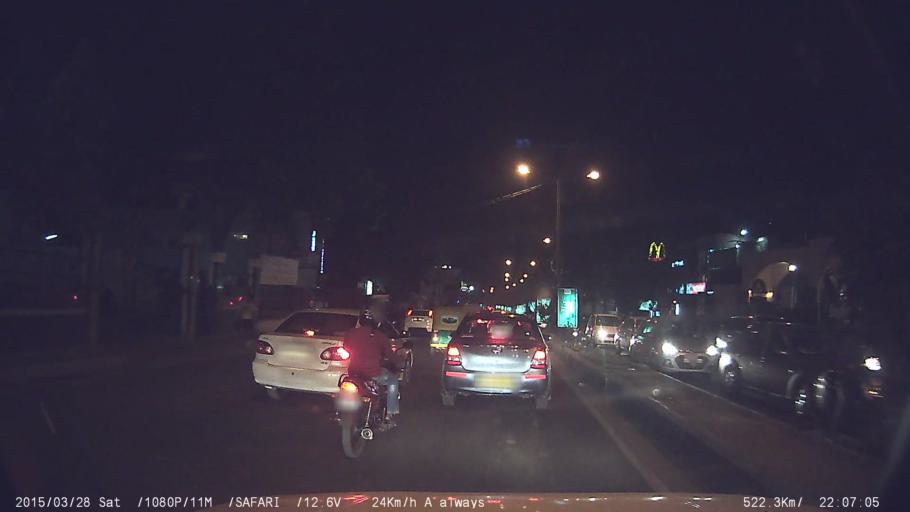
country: IN
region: Karnataka
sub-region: Bangalore Urban
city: Bangalore
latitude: 12.8906
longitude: 77.5981
